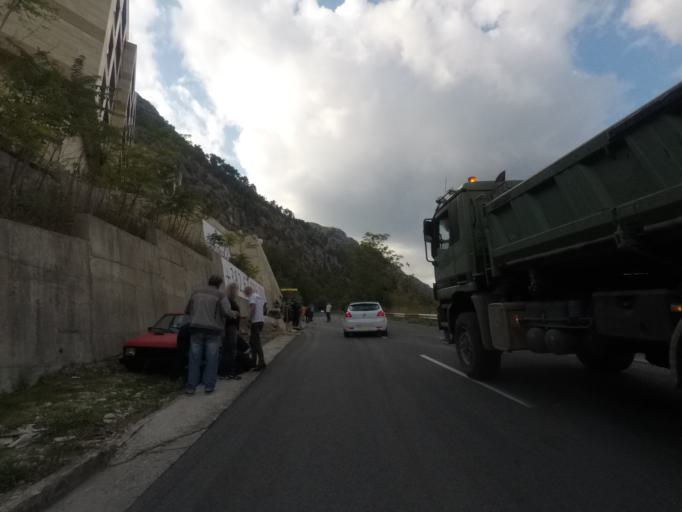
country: ME
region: Kotor
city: Kotor
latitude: 42.4181
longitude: 18.7610
